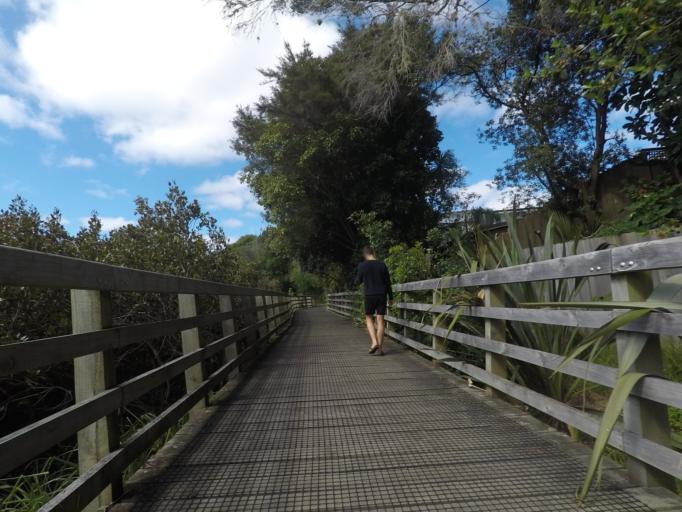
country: NZ
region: Auckland
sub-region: Auckland
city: Auckland
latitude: -36.8520
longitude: 174.7304
